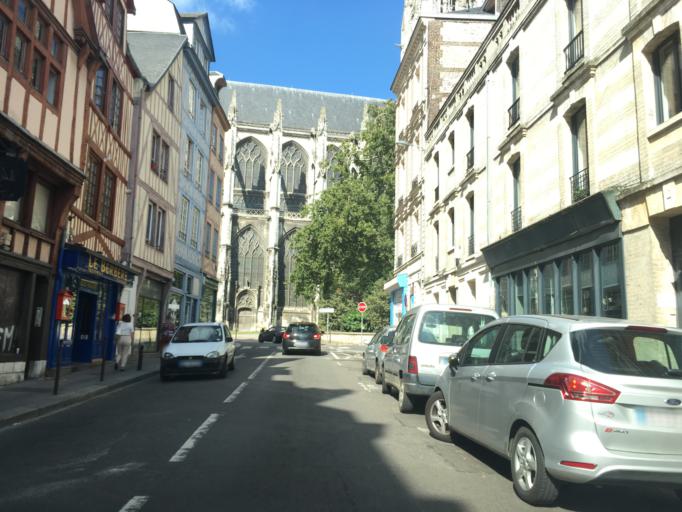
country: FR
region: Haute-Normandie
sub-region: Departement de la Seine-Maritime
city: Rouen
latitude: 49.4417
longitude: 1.0991
